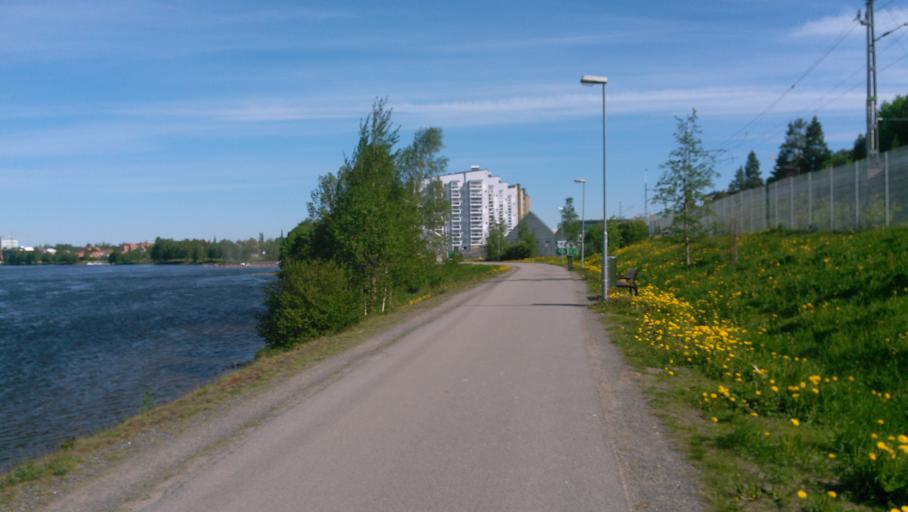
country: SE
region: Vaesterbotten
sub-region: Umea Kommun
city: Umea
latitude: 63.8118
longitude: 20.2948
